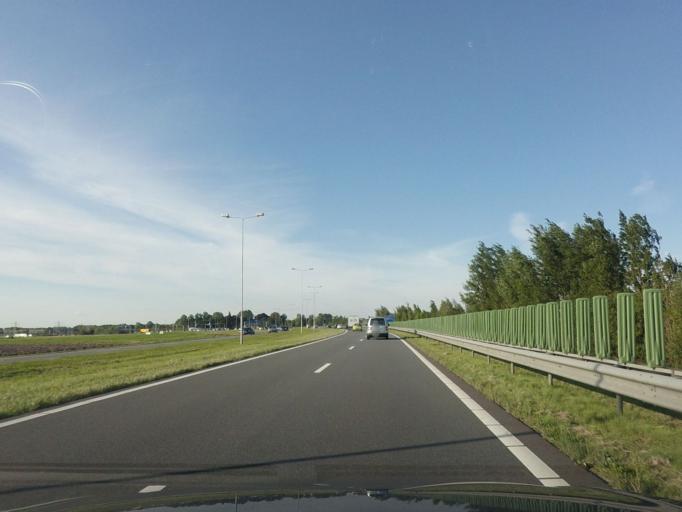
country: NL
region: North Holland
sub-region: Gemeente Haarlemmermeer
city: Hoofddorp
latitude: 52.3637
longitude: 4.7086
